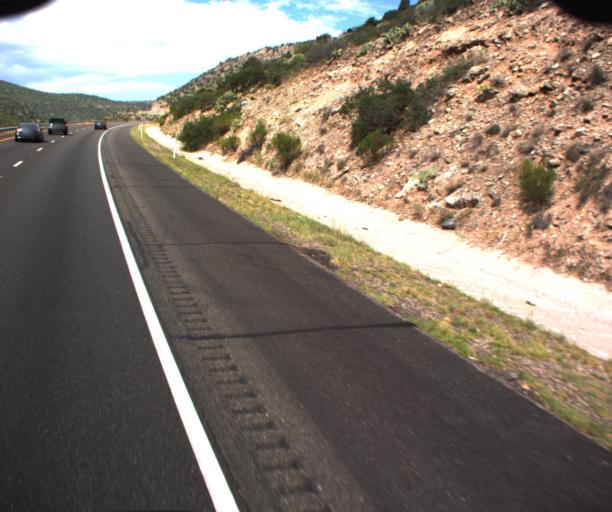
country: US
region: Arizona
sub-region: Yavapai County
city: Camp Verde
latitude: 34.5367
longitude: -111.9283
